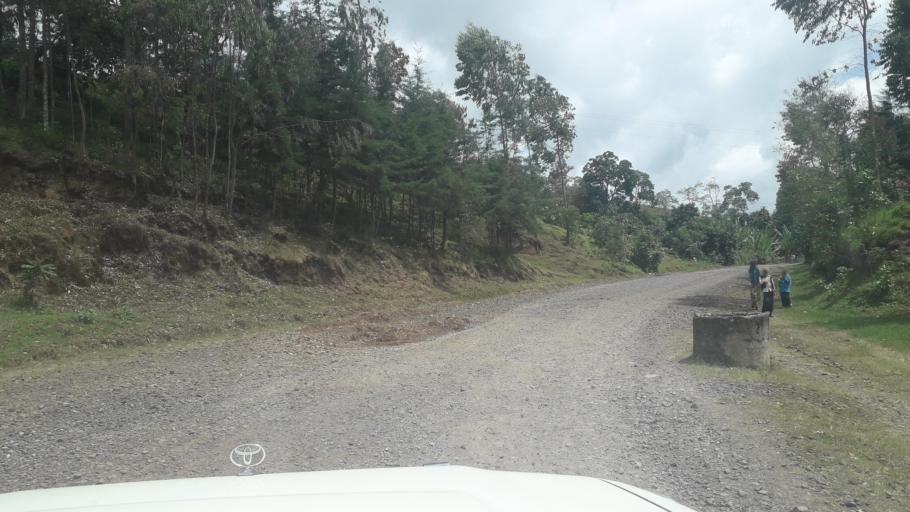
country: ET
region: Oromiya
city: Jima
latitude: 7.4305
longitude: 36.8734
